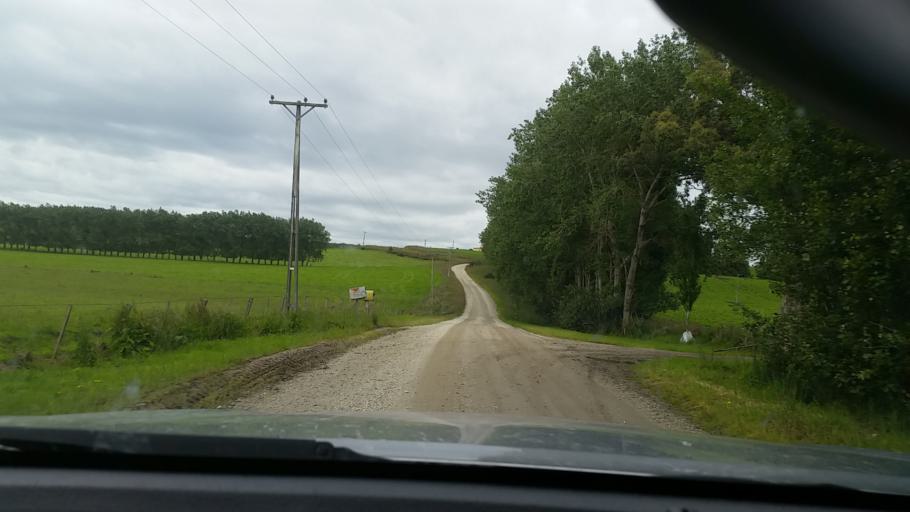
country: NZ
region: Southland
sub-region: Gore District
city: Gore
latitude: -46.2719
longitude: 168.7612
